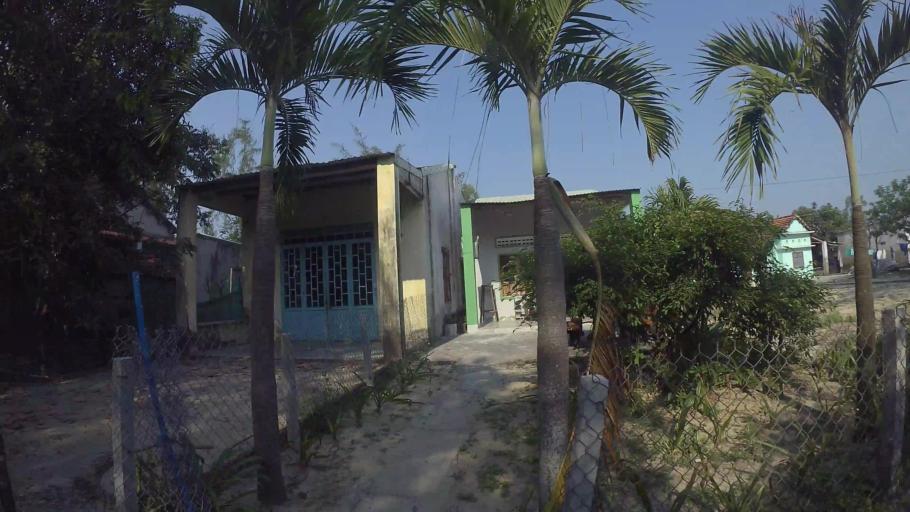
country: VN
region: Quang Nam
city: Quang Nam
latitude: 15.9488
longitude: 108.2694
